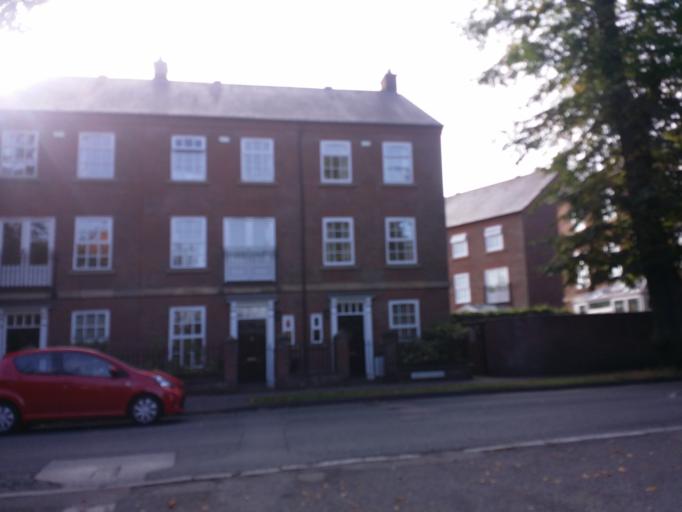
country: GB
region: England
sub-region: City of York
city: York
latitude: 53.9692
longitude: -1.0911
